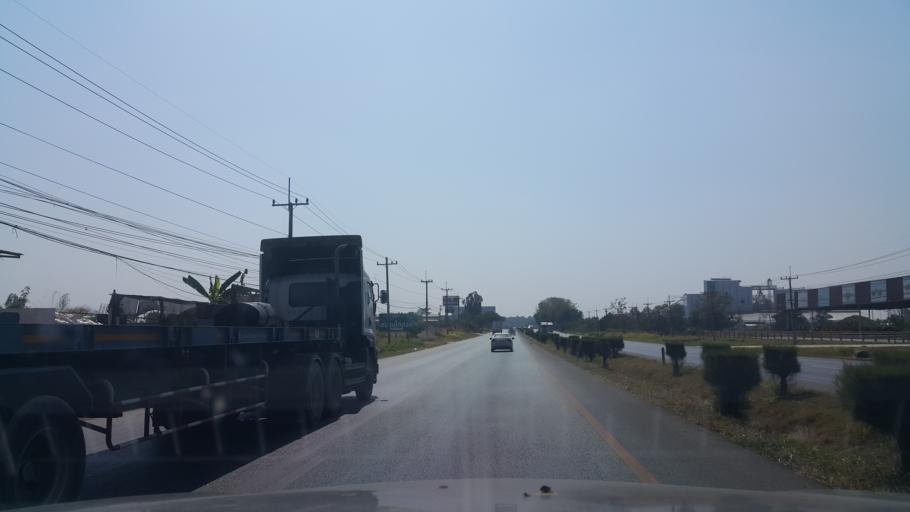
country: TH
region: Khon Kaen
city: Ban Haet
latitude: 16.2929
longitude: 102.7869
